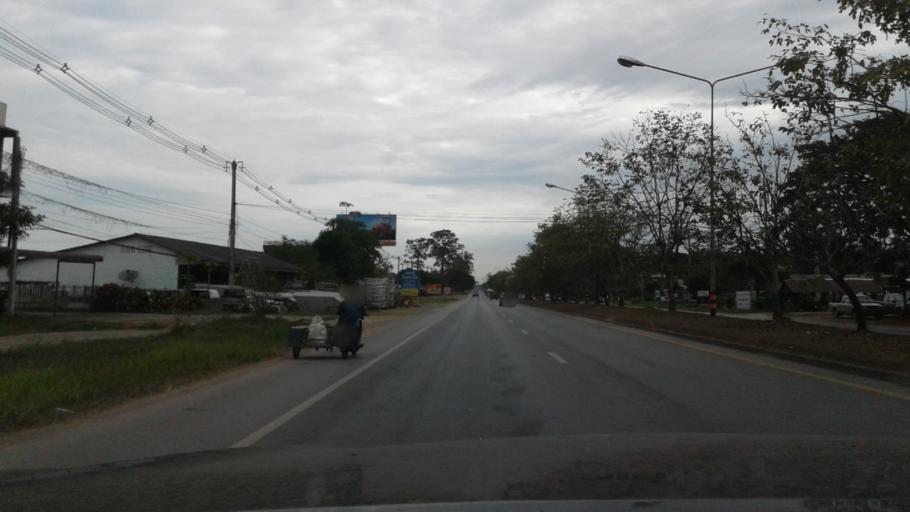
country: TH
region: Changwat Udon Thani
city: Udon Thani
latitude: 17.3637
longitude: 102.7027
